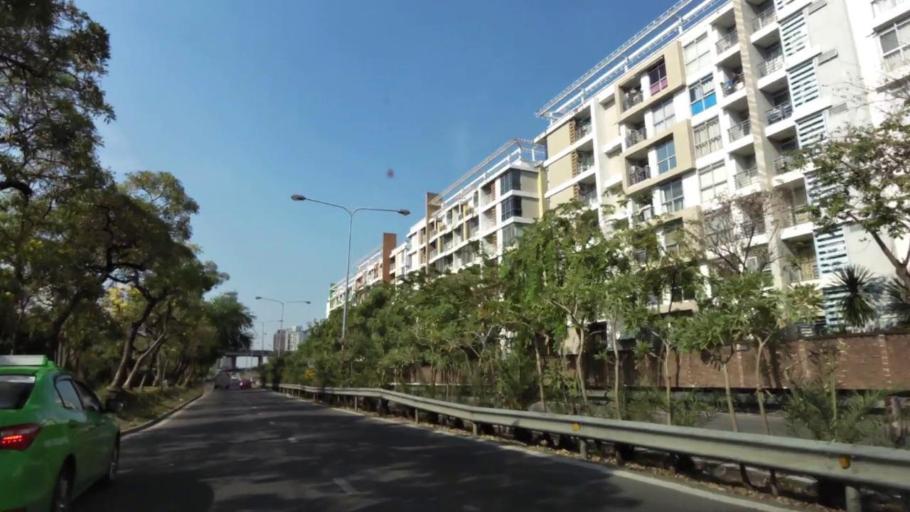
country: TH
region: Bangkok
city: Phra Khanong
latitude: 13.7061
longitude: 100.5978
